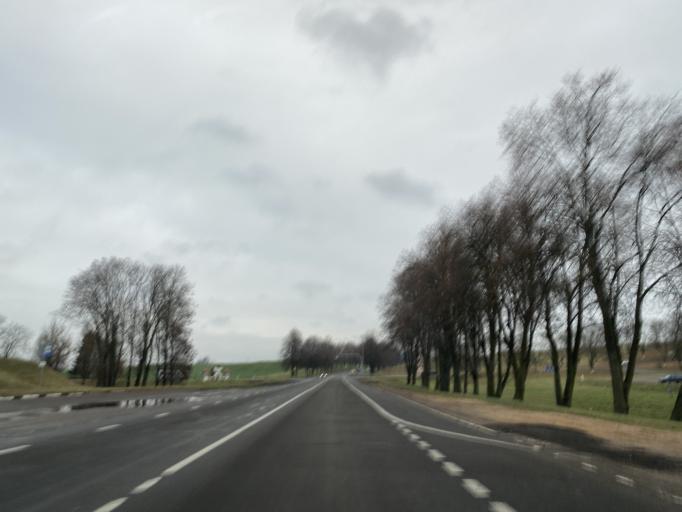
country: BY
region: Minsk
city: Horad Smalyavichy
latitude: 54.0460
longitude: 28.0657
